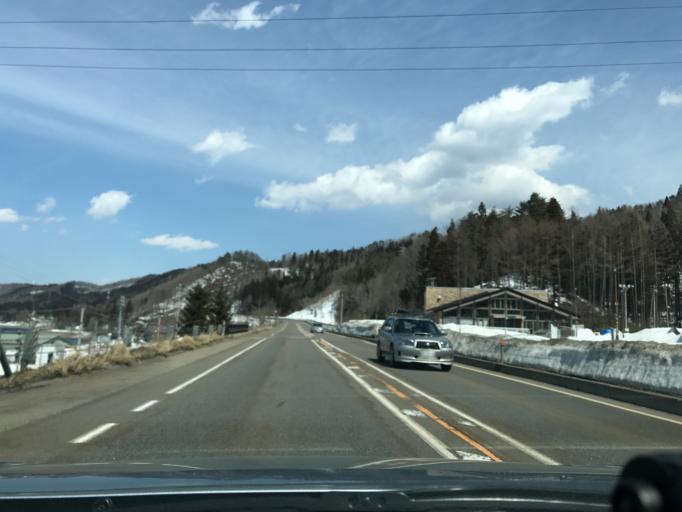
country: JP
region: Nagano
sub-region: Kitaazumi Gun
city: Hakuba
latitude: 36.6047
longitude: 137.8541
